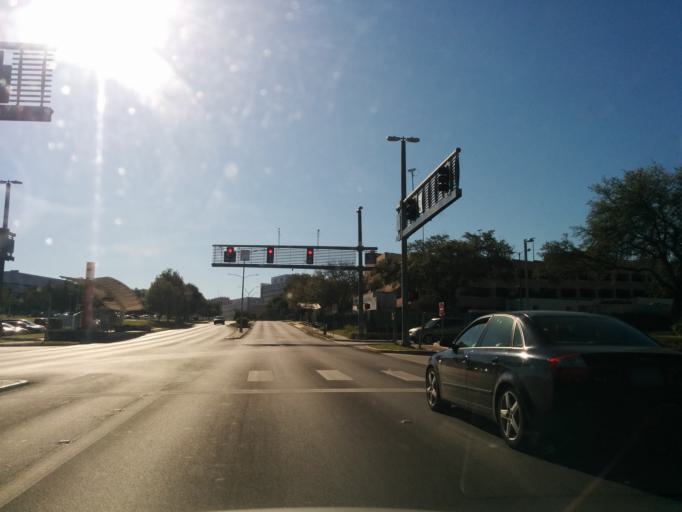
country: US
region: Texas
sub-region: Bexar County
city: Balcones Heights
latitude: 29.5096
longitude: -98.5775
